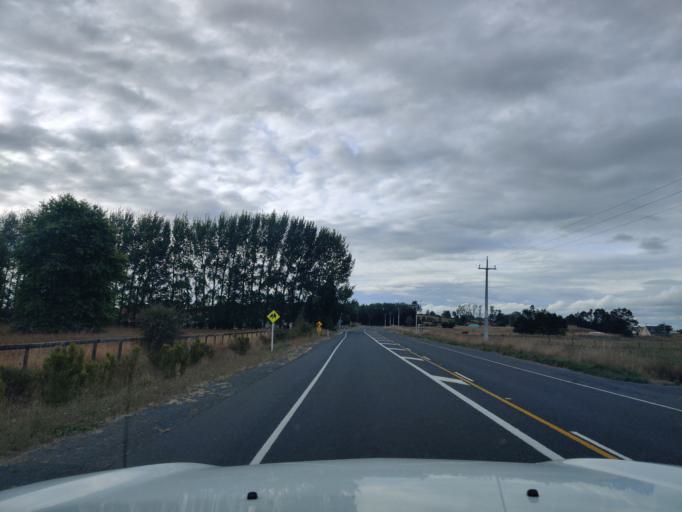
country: NZ
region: Waikato
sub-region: Waipa District
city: Cambridge
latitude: -37.8103
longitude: 175.4520
